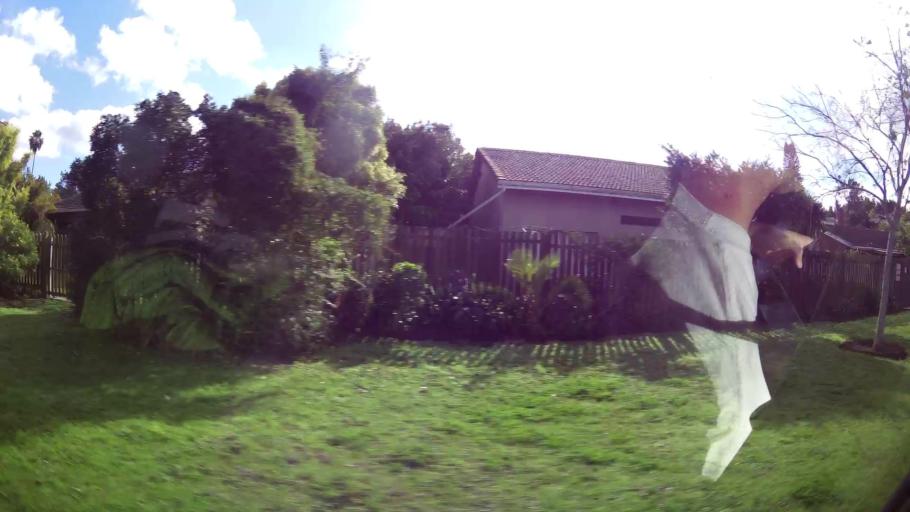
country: ZA
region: Western Cape
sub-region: Eden District Municipality
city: Knysna
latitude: -34.0434
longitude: 23.0702
